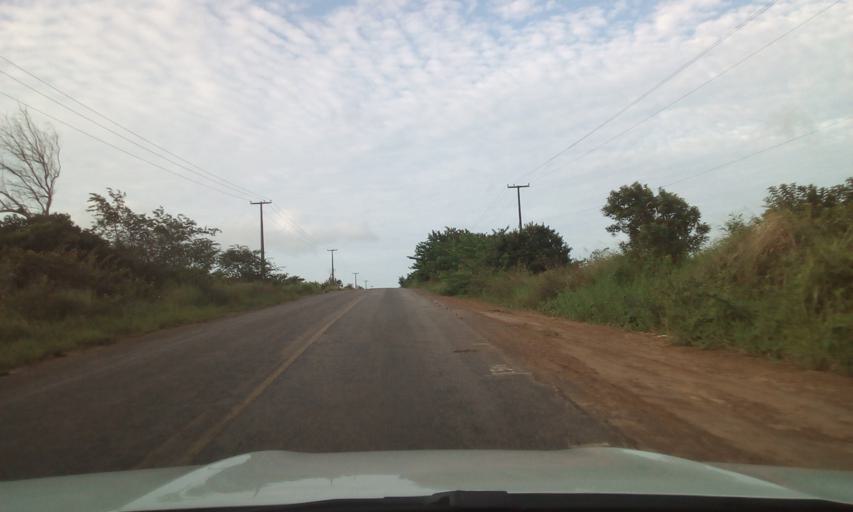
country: BR
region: Paraiba
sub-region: Conde
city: Conde
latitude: -7.2734
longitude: -34.8551
